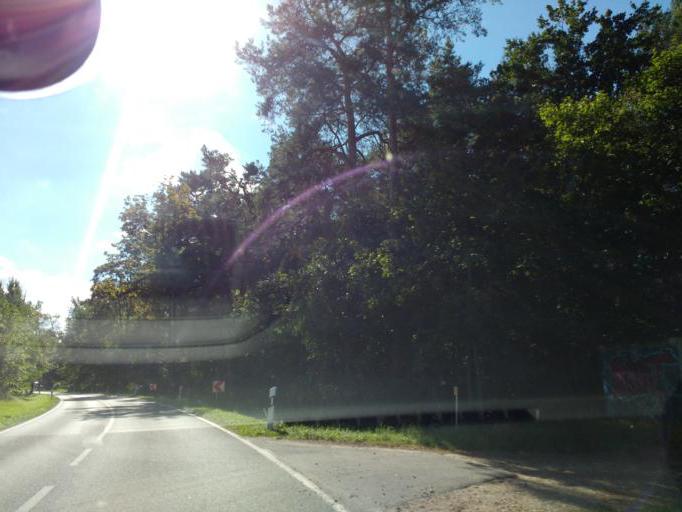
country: DE
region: Brandenburg
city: Mittenwalde
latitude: 52.2258
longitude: 13.5741
